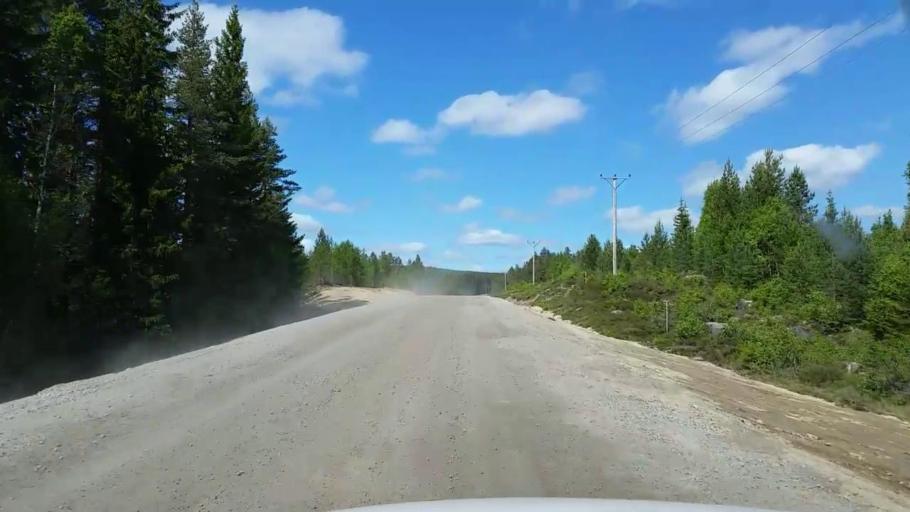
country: SE
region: Gaevleborg
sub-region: Ljusdals Kommun
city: Farila
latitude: 61.5929
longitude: 15.9212
